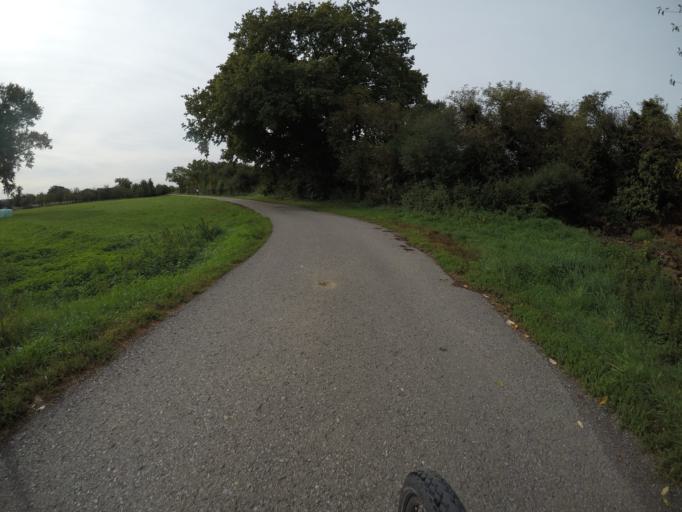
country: DE
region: Baden-Wuerttemberg
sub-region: Karlsruhe Region
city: Kronau
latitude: 49.2335
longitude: 8.6312
